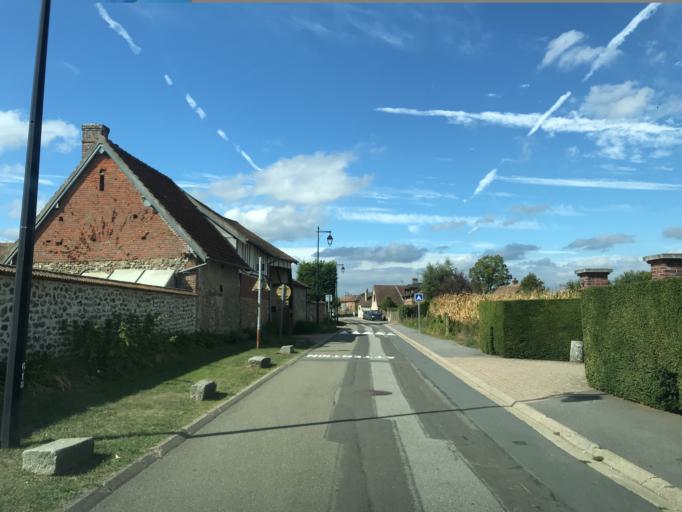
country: FR
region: Haute-Normandie
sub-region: Departement de l'Eure
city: Ande
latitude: 49.1951
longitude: 1.2398
